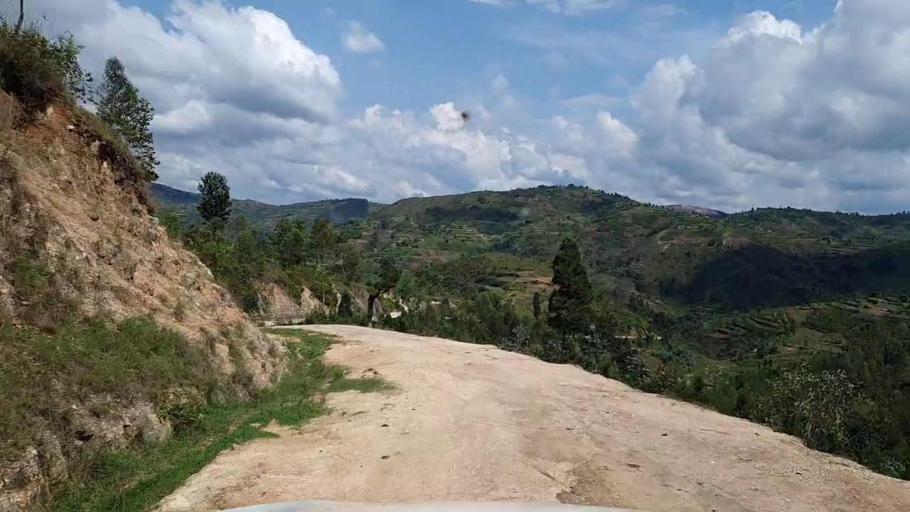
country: RW
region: Southern Province
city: Gikongoro
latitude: -2.3979
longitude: 29.5581
